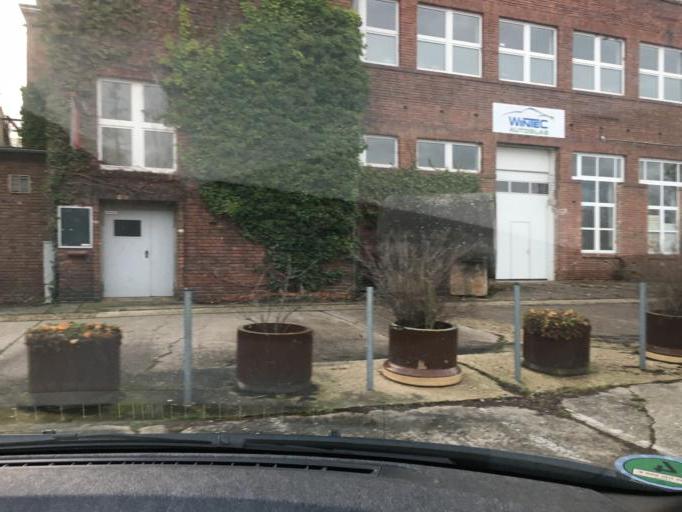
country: DE
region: North Rhine-Westphalia
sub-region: Regierungsbezirk Koln
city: Mechernich
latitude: 50.6310
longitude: 6.6847
